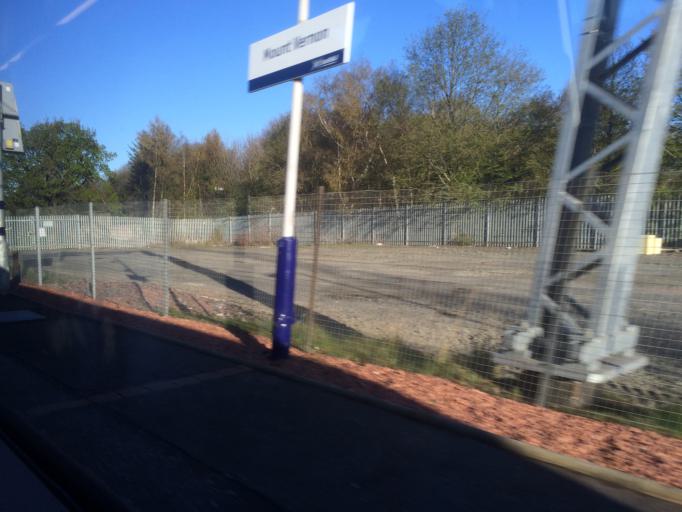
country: GB
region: Scotland
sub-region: North Lanarkshire
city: Stepps
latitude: 55.8405
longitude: -4.1327
